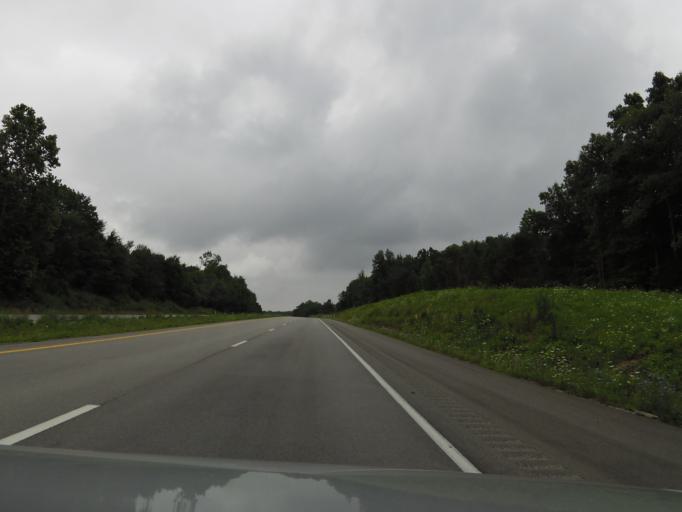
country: US
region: Kentucky
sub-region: Grayson County
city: Leitchfield
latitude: 37.4091
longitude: -86.4713
